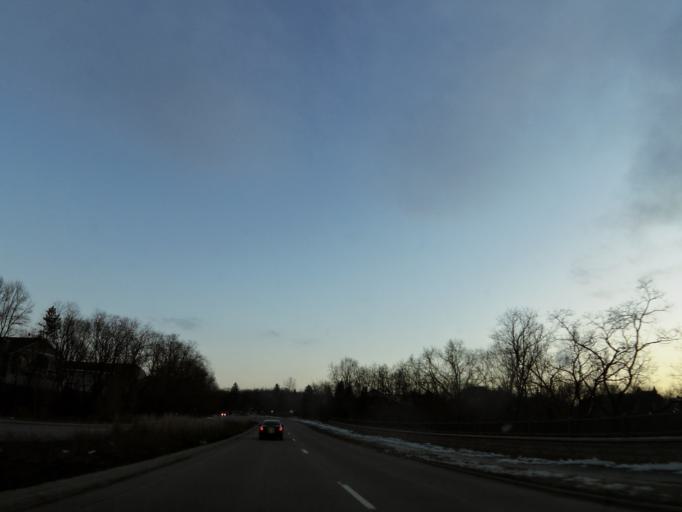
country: US
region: Minnesota
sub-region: Hennepin County
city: Minnetonka Mills
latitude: 44.9048
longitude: -93.4276
